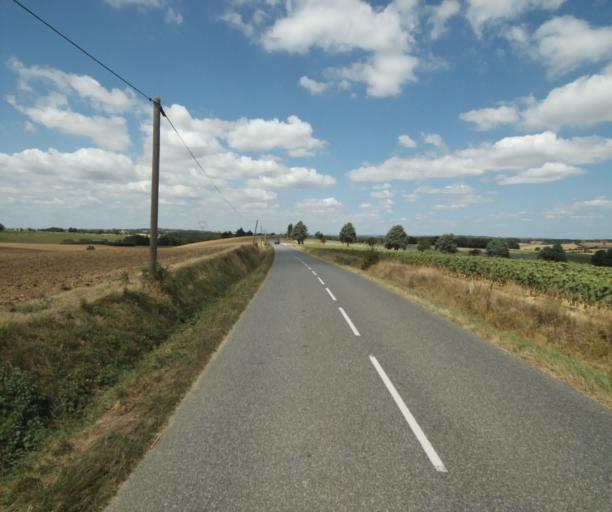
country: FR
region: Midi-Pyrenees
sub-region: Departement de la Haute-Garonne
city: Auriac-sur-Vendinelle
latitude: 43.4644
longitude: 1.8240
